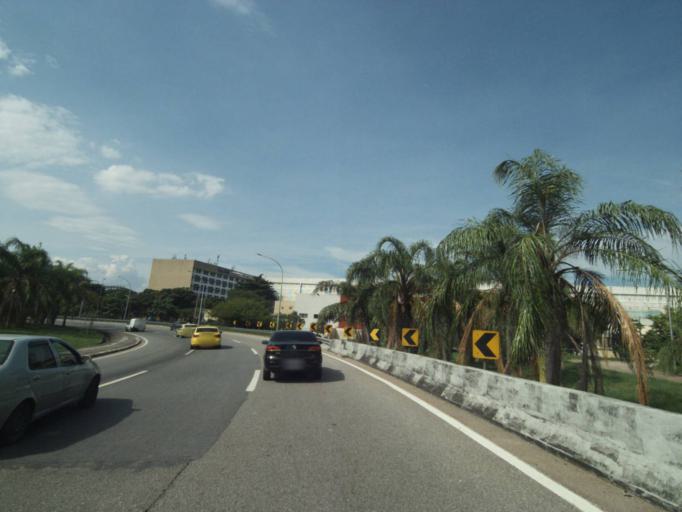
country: BR
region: Rio de Janeiro
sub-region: Rio De Janeiro
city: Rio de Janeiro
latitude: -22.8617
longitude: -43.2322
